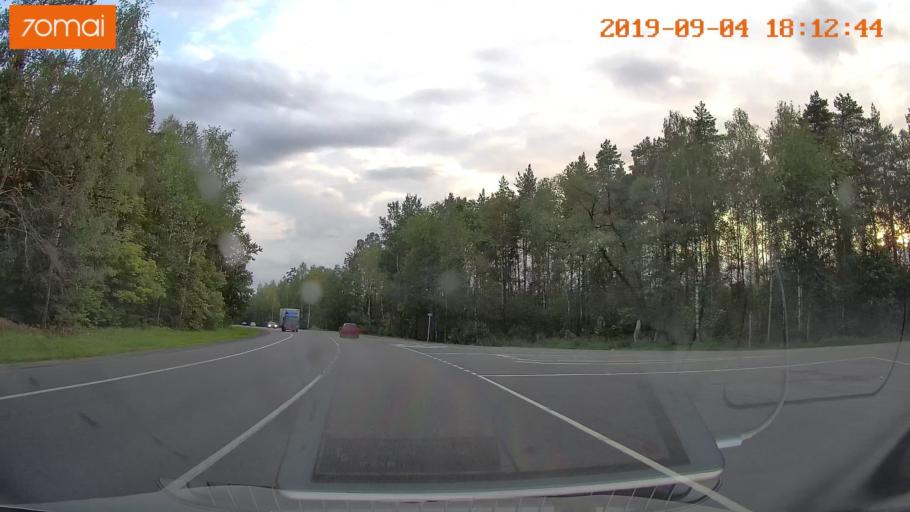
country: RU
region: Moskovskaya
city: Lopatinskiy
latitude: 55.3681
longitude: 38.7379
